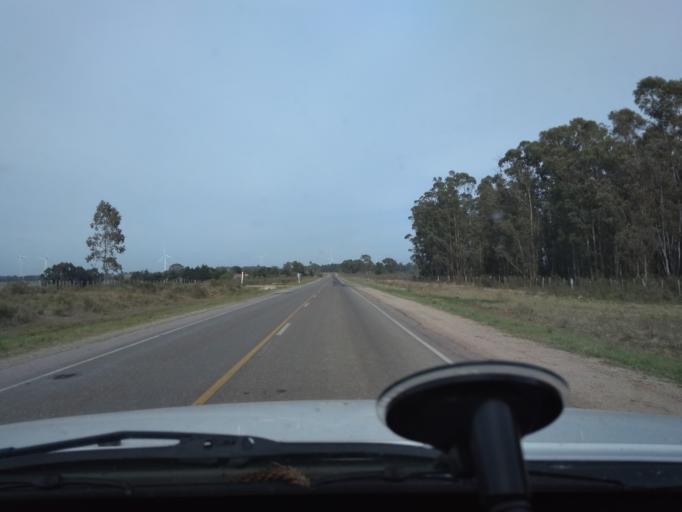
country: UY
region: Florida
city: Florida
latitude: -34.0731
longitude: -56.0724
